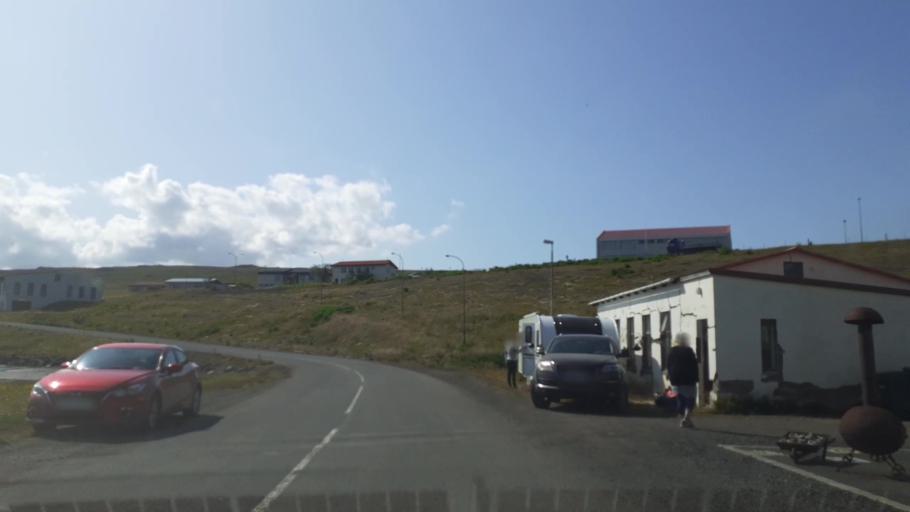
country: IS
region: West
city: Borgarnes
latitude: 65.2088
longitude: -21.0959
